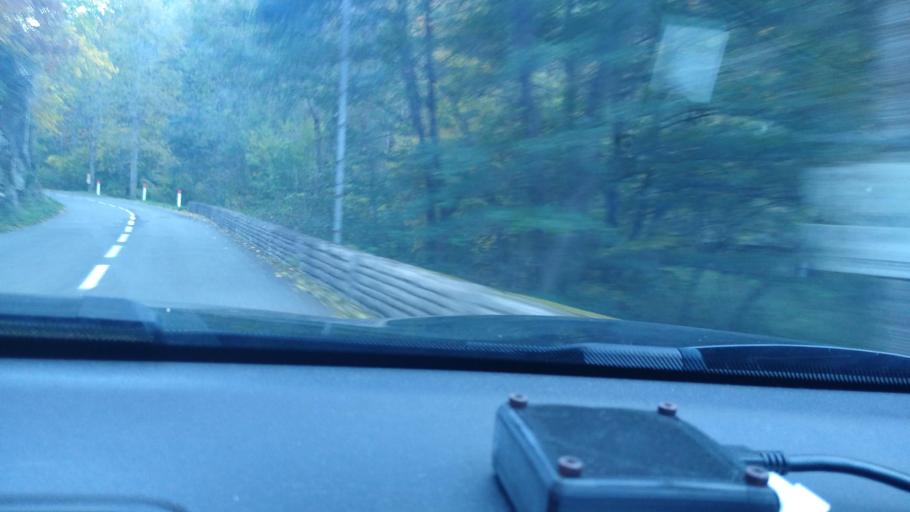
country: FR
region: Languedoc-Roussillon
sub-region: Departement de l'Aude
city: Quillan
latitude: 42.7281
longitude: 2.1072
